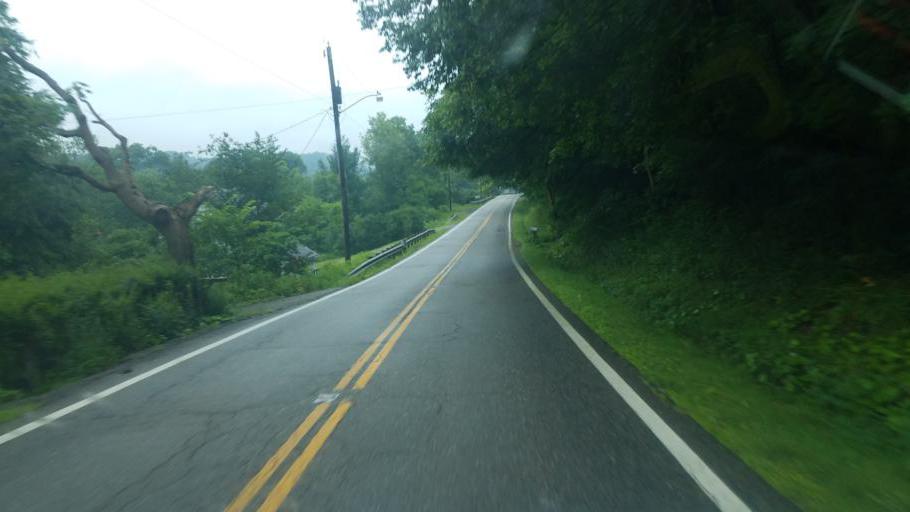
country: US
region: Ohio
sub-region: Columbiana County
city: Salineville
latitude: 40.4672
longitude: -80.9335
